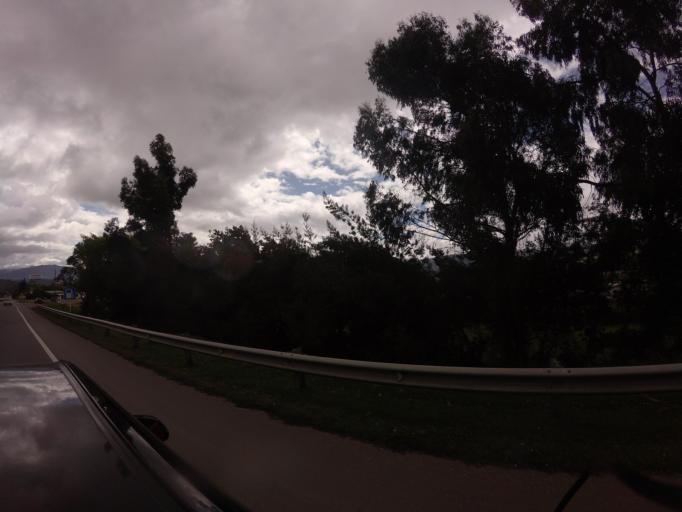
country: CO
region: Cundinamarca
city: Sesquile
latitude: 5.0596
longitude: -73.7775
